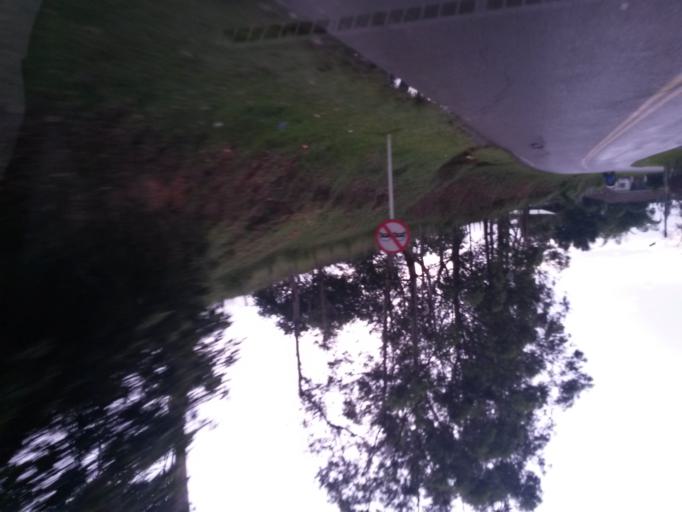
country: CO
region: Cauca
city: Popayan
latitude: 2.4620
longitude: -76.6529
